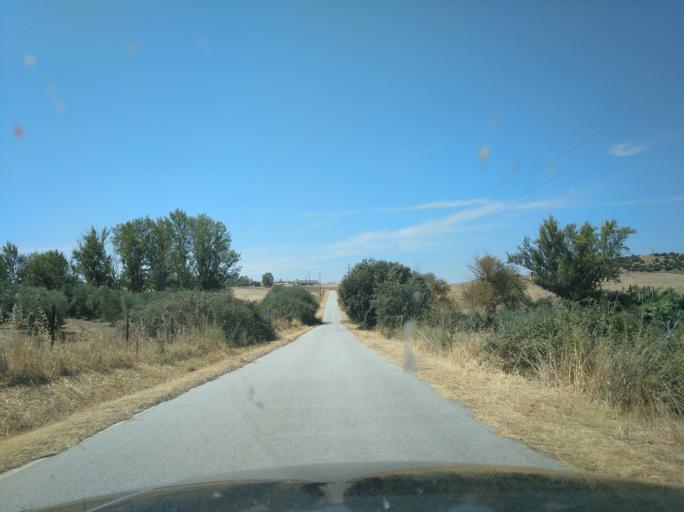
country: PT
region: Portalegre
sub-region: Campo Maior
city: Campo Maior
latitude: 38.9614
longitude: -7.1088
